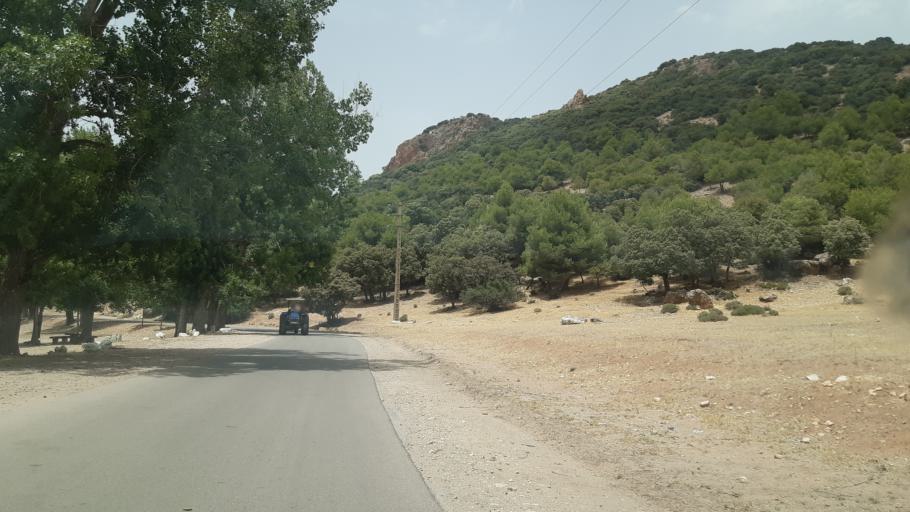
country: MA
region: Meknes-Tafilalet
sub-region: Ifrane
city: Ifrane
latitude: 33.6545
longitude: -5.0345
